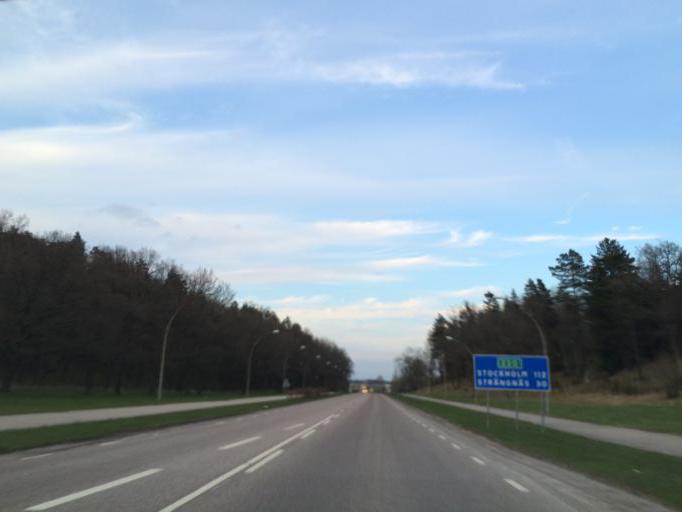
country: SE
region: Soedermanland
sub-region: Eskilstuna Kommun
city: Eskilstuna
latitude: 59.3668
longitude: 16.5415
